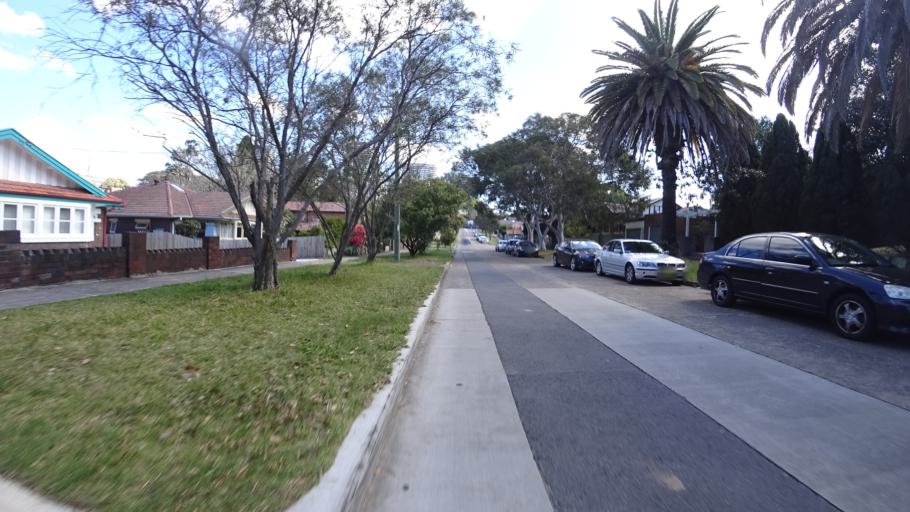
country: AU
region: New South Wales
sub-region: Willoughby
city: Chatswood
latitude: -33.7921
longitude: 151.1858
